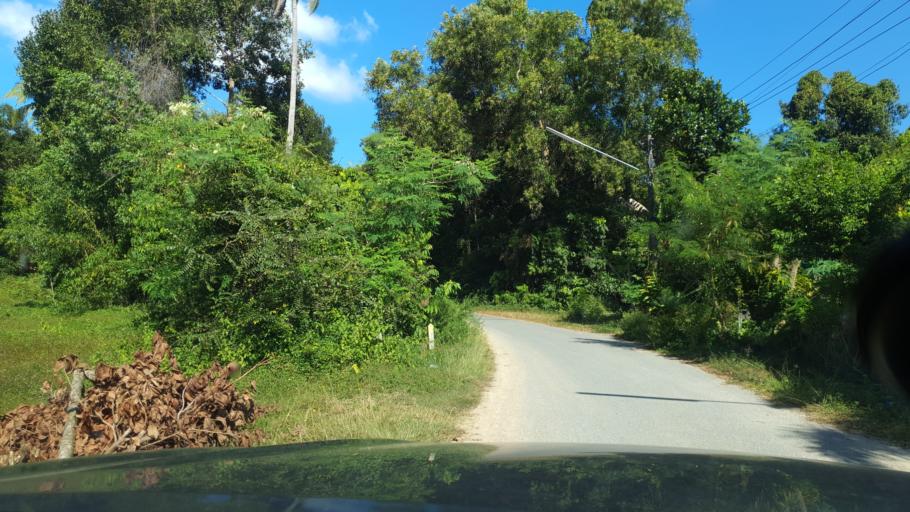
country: TH
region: Krabi
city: Krabi
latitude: 8.0226
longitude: 98.8795
